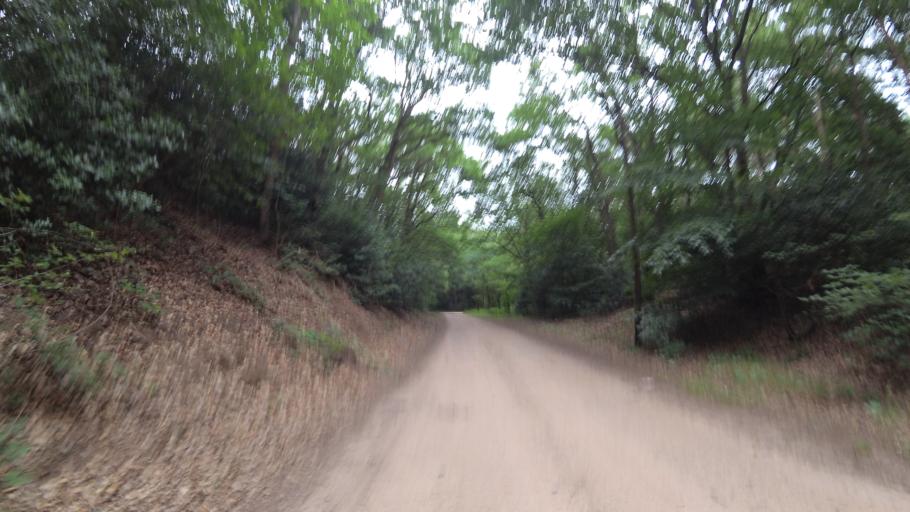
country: DE
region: Lower Saxony
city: Fresenburg
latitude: 52.8806
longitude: 7.3009
